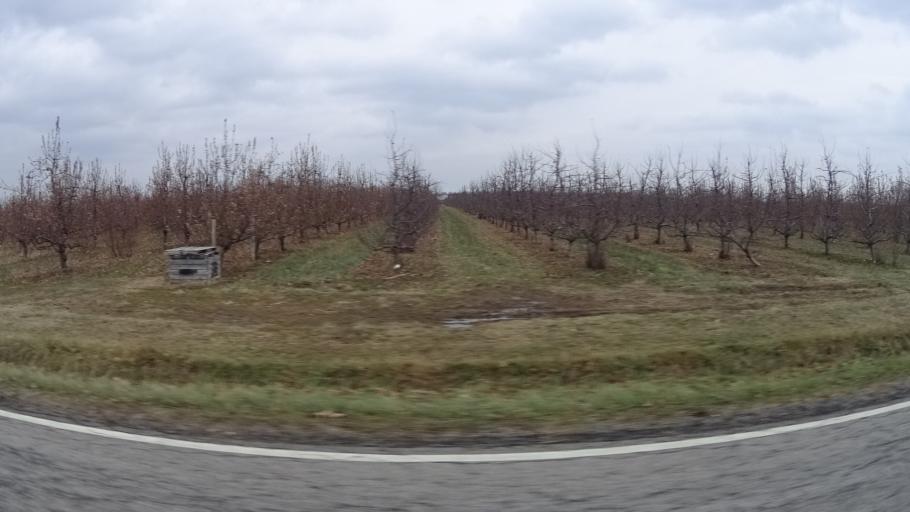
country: US
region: Ohio
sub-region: Lorain County
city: Amherst
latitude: 41.3641
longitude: -82.1753
